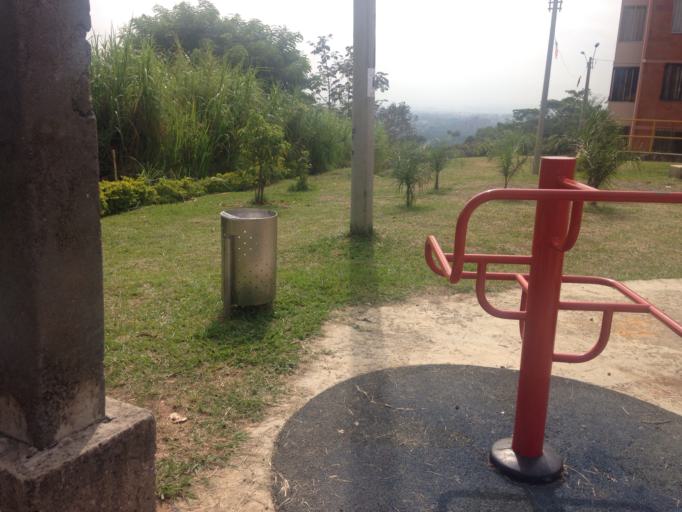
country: CO
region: Valle del Cauca
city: Cali
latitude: 3.3817
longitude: -76.5576
